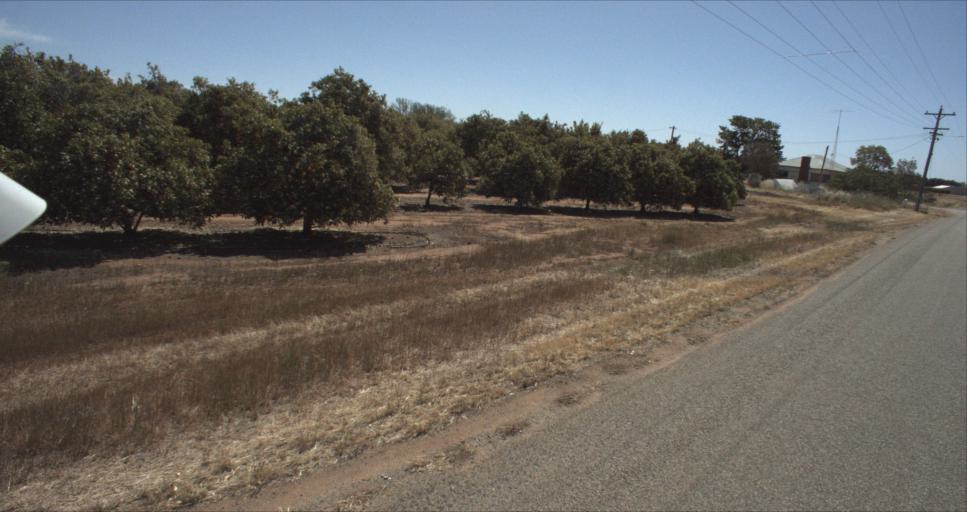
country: AU
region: New South Wales
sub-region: Leeton
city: Leeton
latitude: -34.5432
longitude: 146.3532
